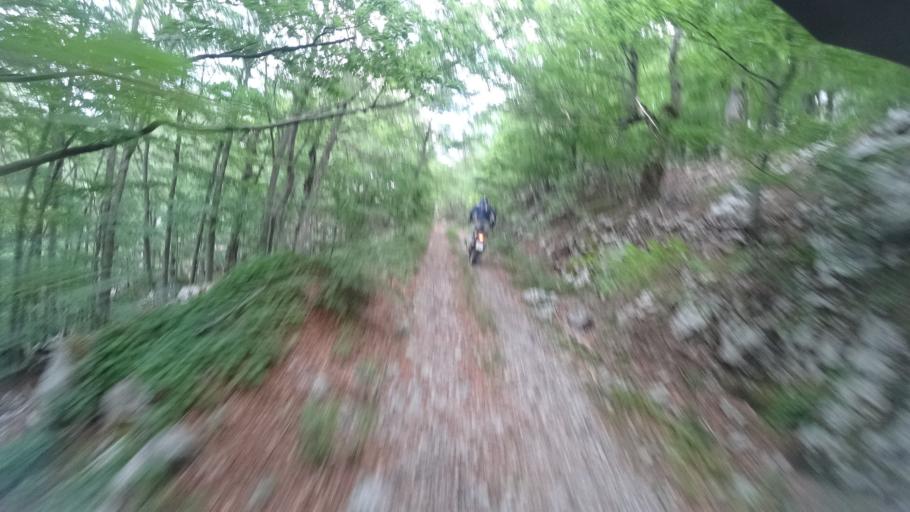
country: HR
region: Licko-Senjska
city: Gospic
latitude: 44.4313
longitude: 15.2883
